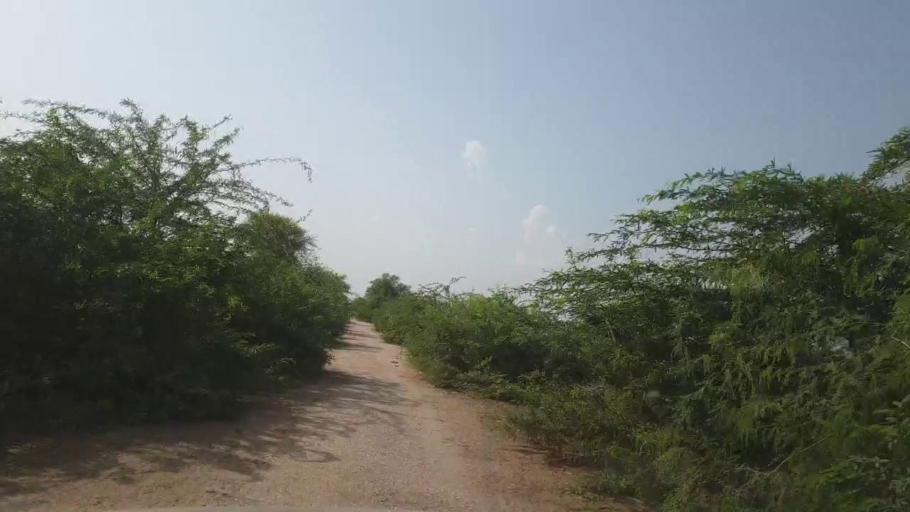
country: PK
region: Sindh
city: Pano Aqil
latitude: 27.7713
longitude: 69.1656
